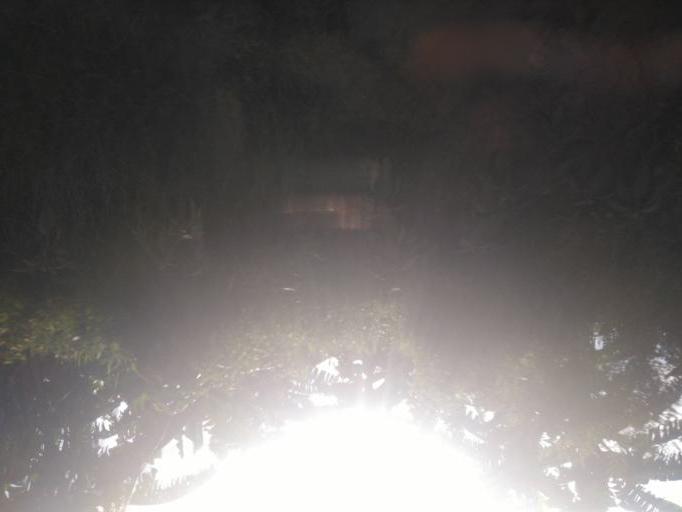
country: UG
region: Central Region
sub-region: Wakiso District
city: Kajansi
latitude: 0.2926
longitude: 32.4535
